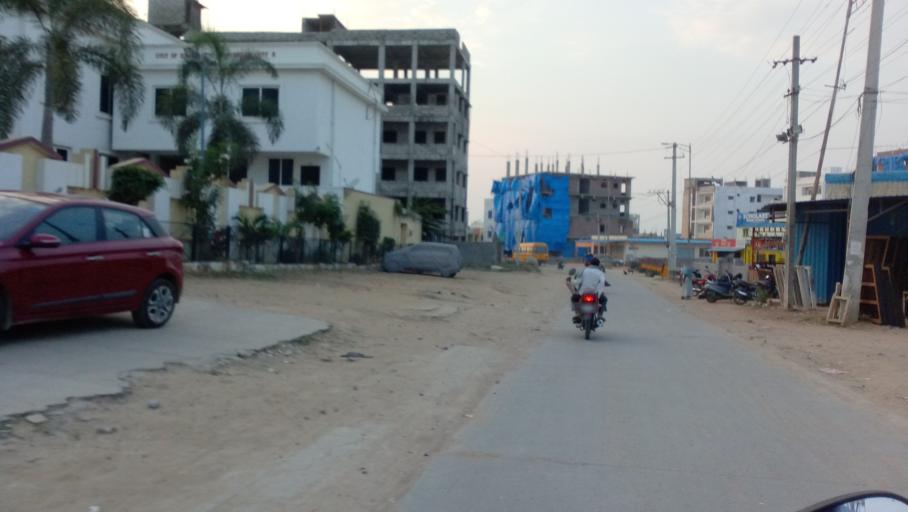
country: IN
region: Telangana
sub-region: Medak
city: Serilingampalle
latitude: 17.5219
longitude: 78.3021
